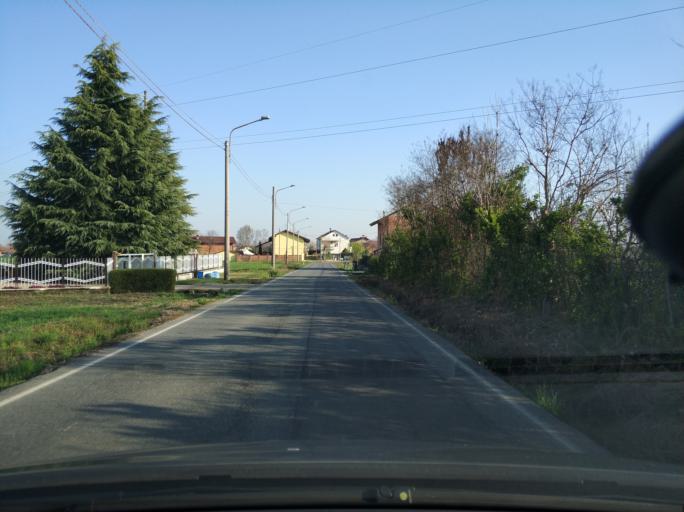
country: IT
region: Piedmont
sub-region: Provincia di Torino
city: Cirie
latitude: 45.2087
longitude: 7.5968
